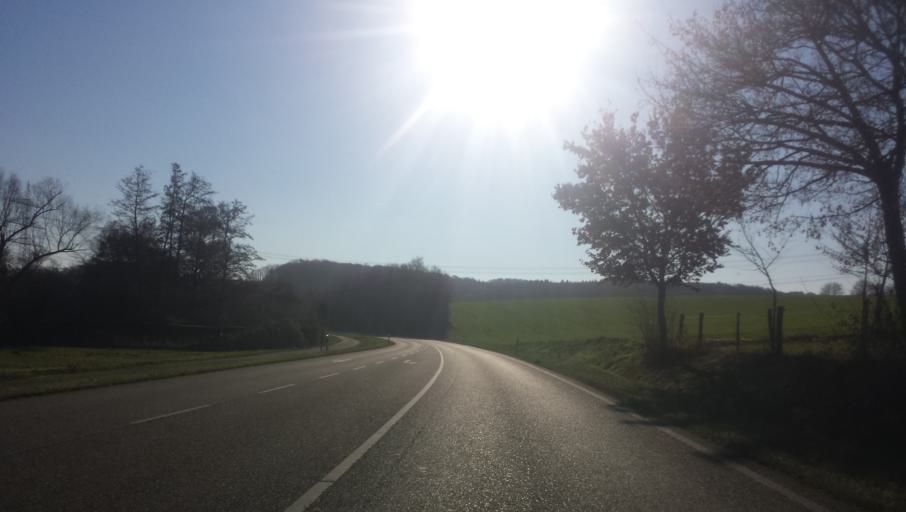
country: DE
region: Baden-Wuerttemberg
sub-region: Karlsruhe Region
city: Neidenstein
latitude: 49.3105
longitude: 8.8871
